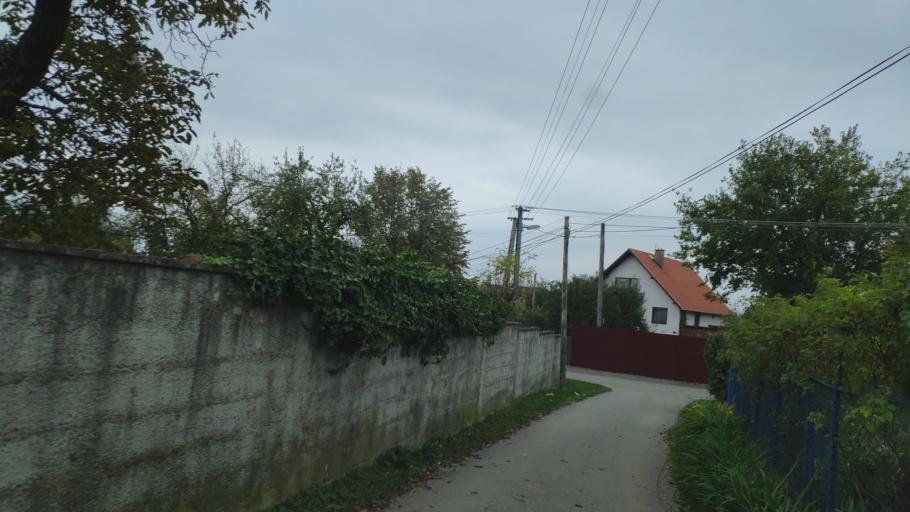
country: SK
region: Kosicky
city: Kosice
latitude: 48.6335
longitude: 21.3941
